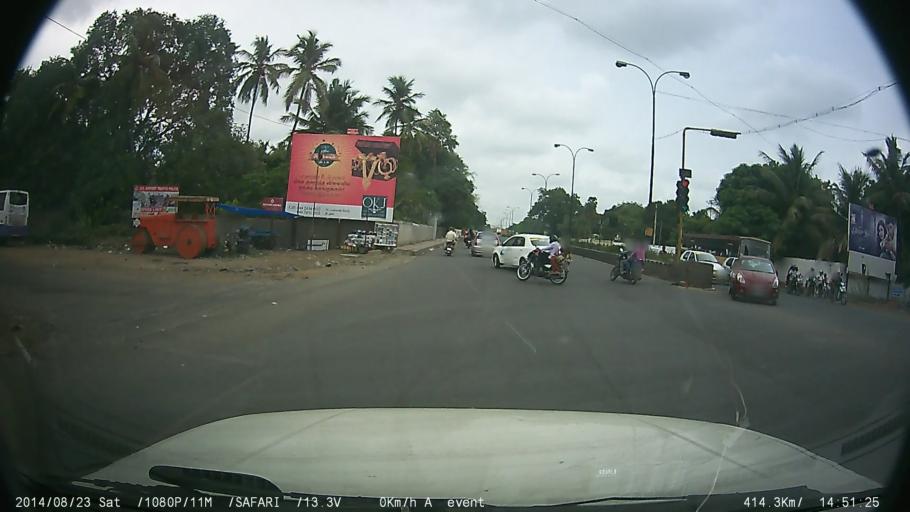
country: IN
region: Tamil Nadu
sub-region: Kancheepuram
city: Pallavaram
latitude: 12.9733
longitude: 80.1529
